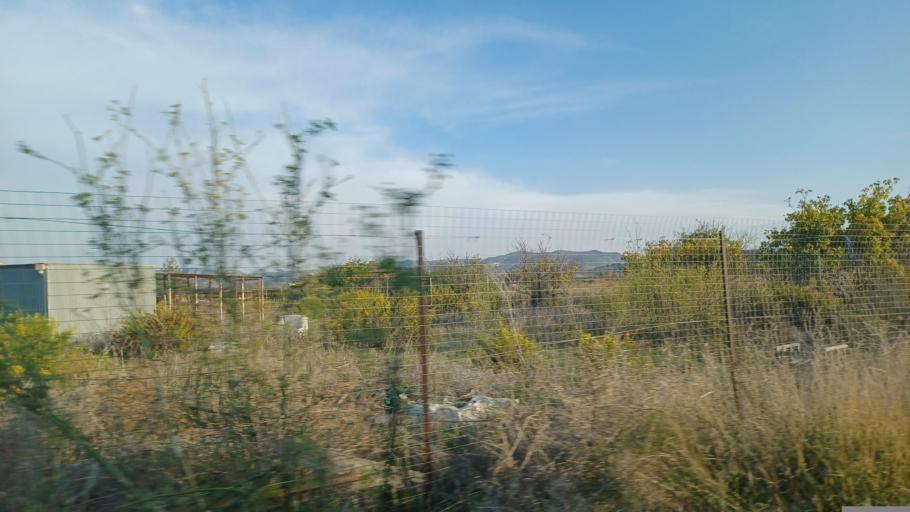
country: CY
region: Pafos
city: Kissonerga
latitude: 34.8322
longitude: 32.4006
